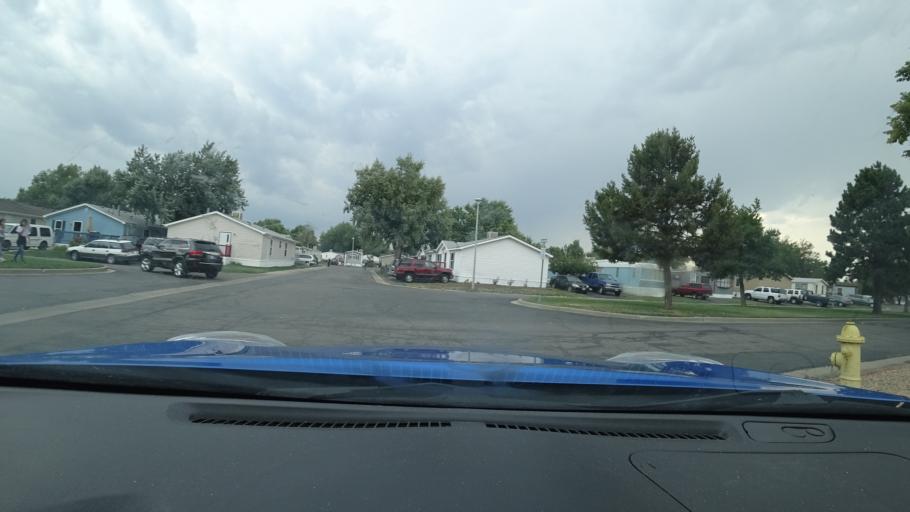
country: US
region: Colorado
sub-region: Adams County
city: Aurora
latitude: 39.7436
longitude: -104.7846
